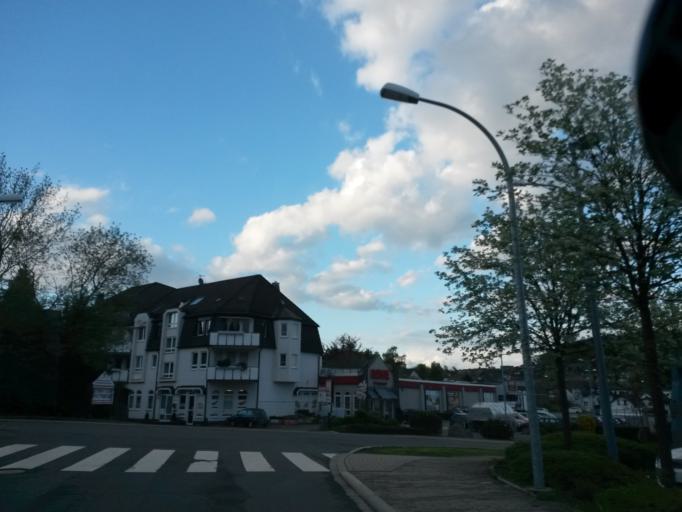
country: DE
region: North Rhine-Westphalia
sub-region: Regierungsbezirk Arnsberg
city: Herscheid
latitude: 51.1774
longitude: 7.7450
